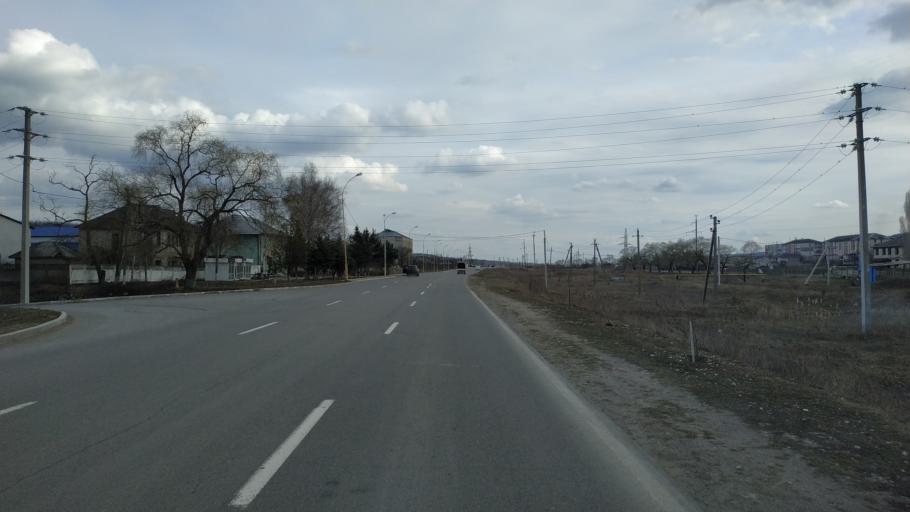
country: MD
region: Hincesti
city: Hincesti
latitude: 46.8263
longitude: 28.6037
